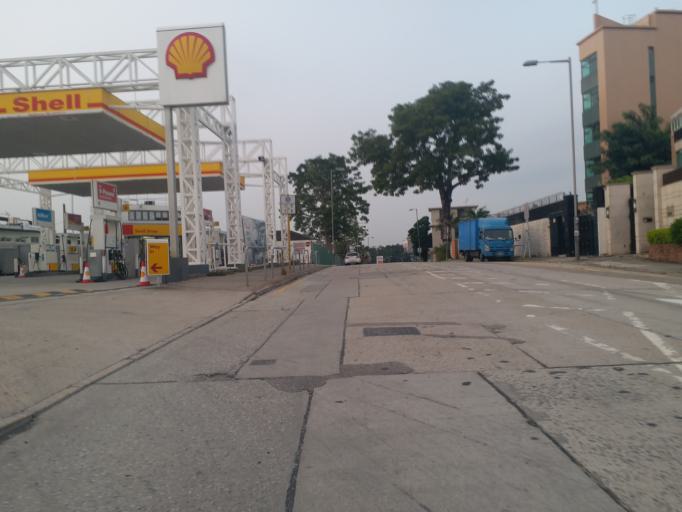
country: HK
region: Yuen Long
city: Yuen Long Kau Hui
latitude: 22.4395
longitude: 114.0110
